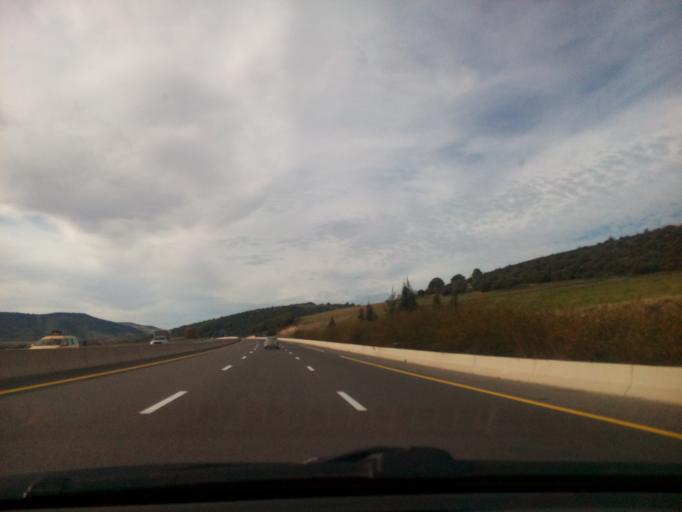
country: DZ
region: Sidi Bel Abbes
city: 'Ain el Berd
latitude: 35.4241
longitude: -0.4698
